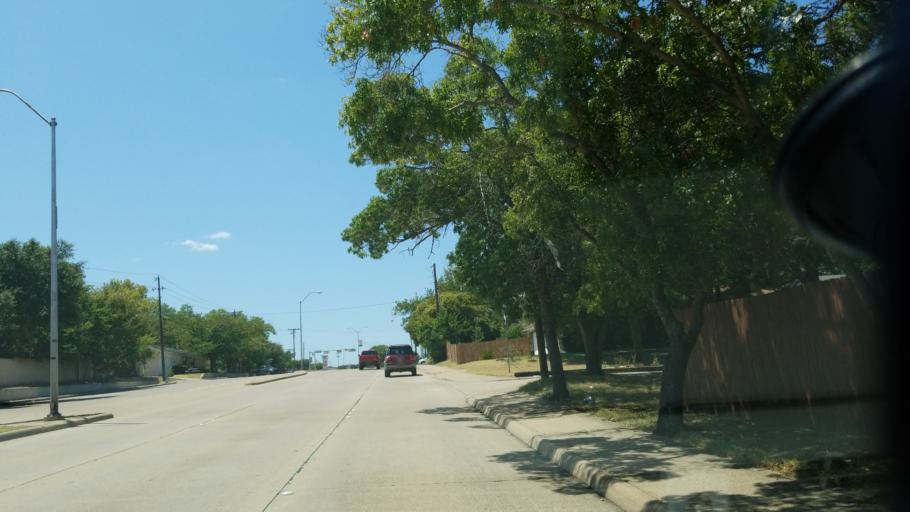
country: US
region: Texas
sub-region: Dallas County
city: Duncanville
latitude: 32.6475
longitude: -96.8977
